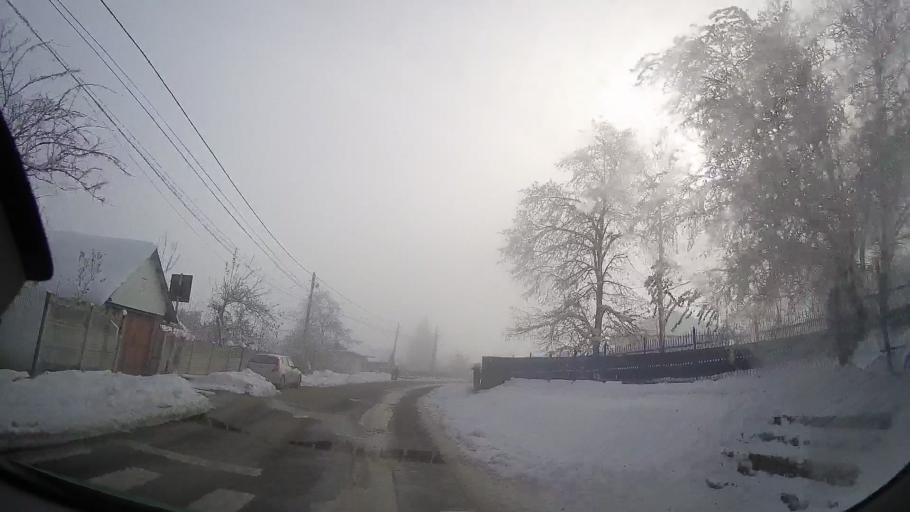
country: RO
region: Iasi
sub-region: Comuna Valea Seaca
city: Topile
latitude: 47.2454
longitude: 26.6645
